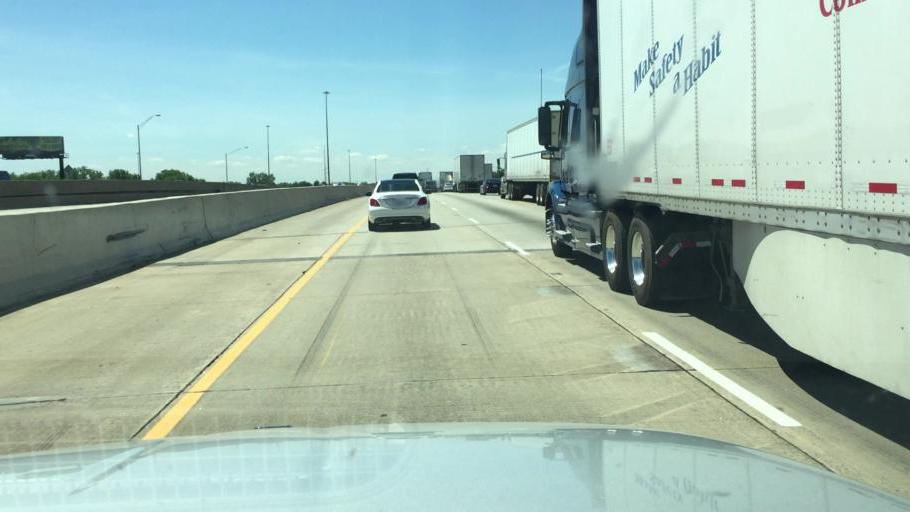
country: US
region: Indiana
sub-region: Lake County
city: Highland
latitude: 41.5702
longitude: -87.4222
